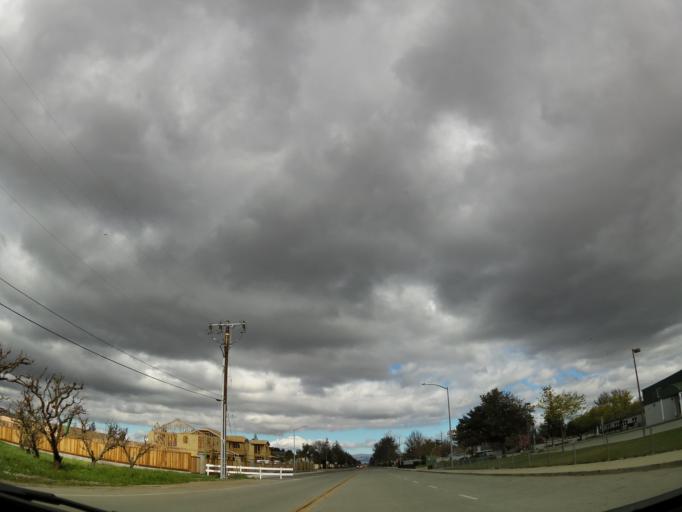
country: US
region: California
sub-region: San Benito County
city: Hollister
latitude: 36.8288
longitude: -121.3933
